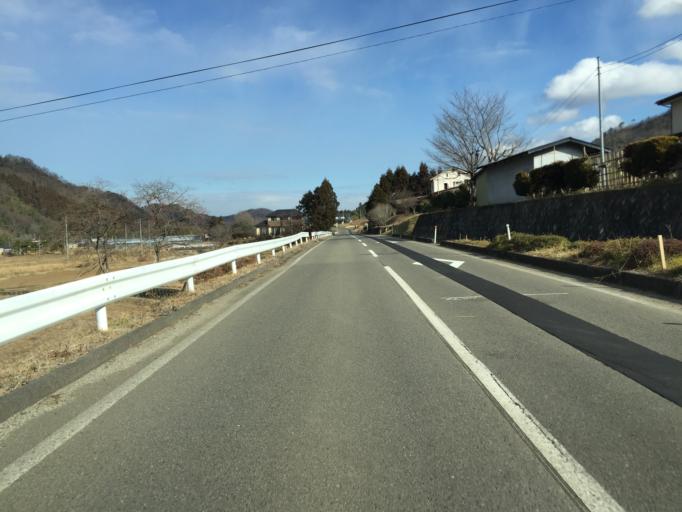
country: JP
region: Fukushima
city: Hobaramachi
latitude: 37.7440
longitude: 140.5632
